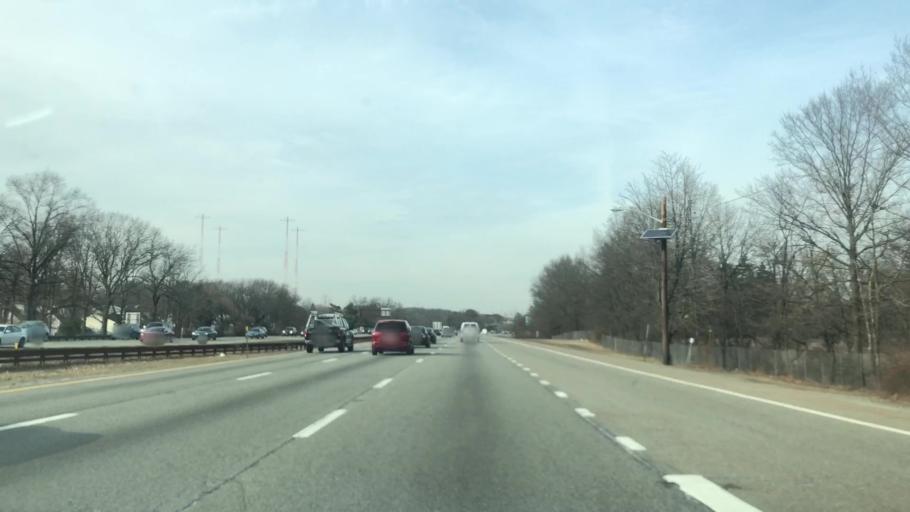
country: US
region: New Jersey
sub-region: Essex County
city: Brookdale
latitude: 40.8403
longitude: -74.1831
